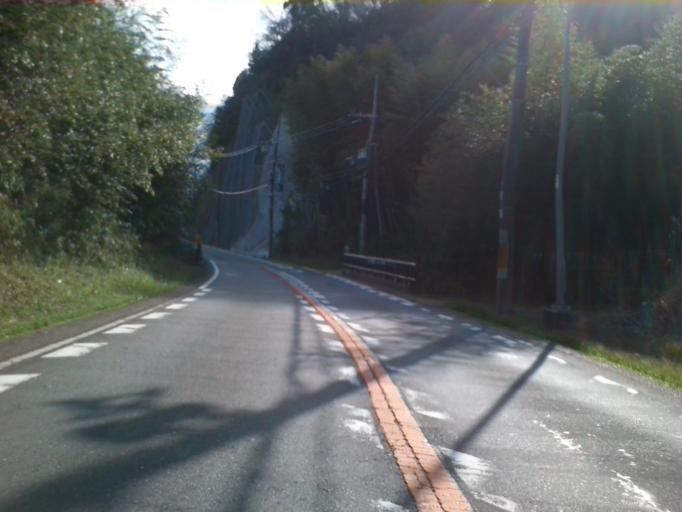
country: JP
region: Nara
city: Nara-shi
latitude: 34.7607
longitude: 135.8444
